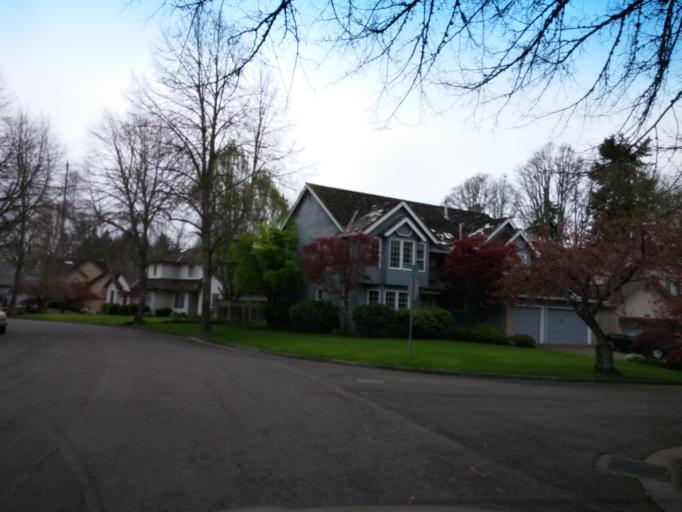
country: US
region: Oregon
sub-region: Washington County
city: Oak Hills
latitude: 45.5272
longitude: -122.8439
